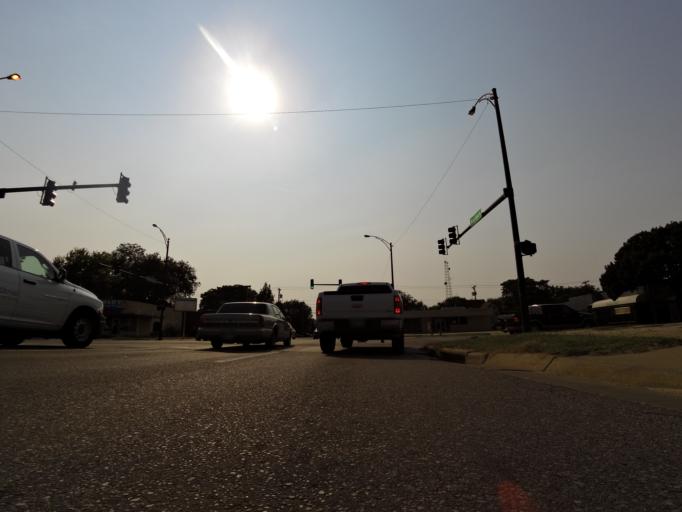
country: US
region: Kansas
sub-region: Sedgwick County
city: Wichita
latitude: 37.6976
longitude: -97.3353
